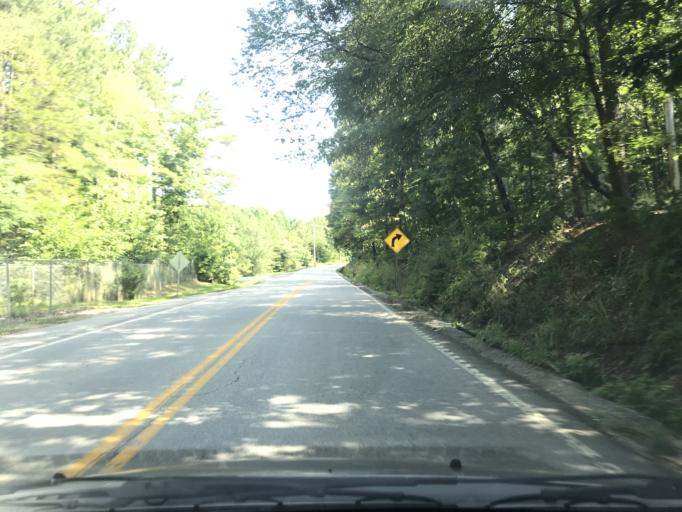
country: US
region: Tennessee
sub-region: Hamilton County
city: Lakesite
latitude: 35.1971
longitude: -85.0709
